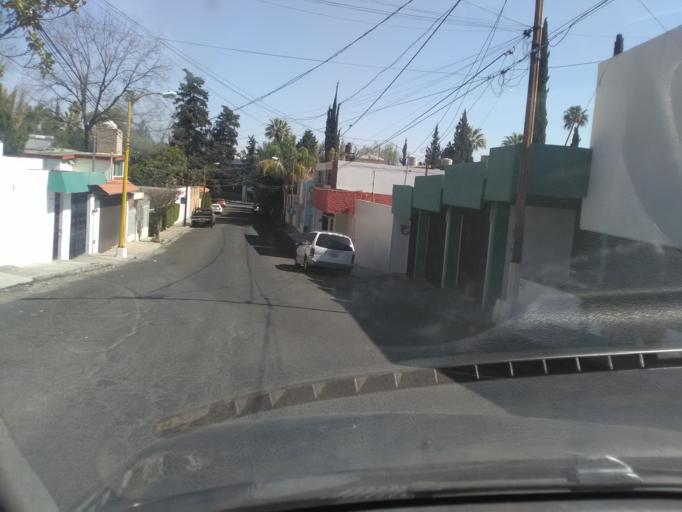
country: MX
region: Durango
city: Victoria de Durango
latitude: 24.0243
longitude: -104.6816
